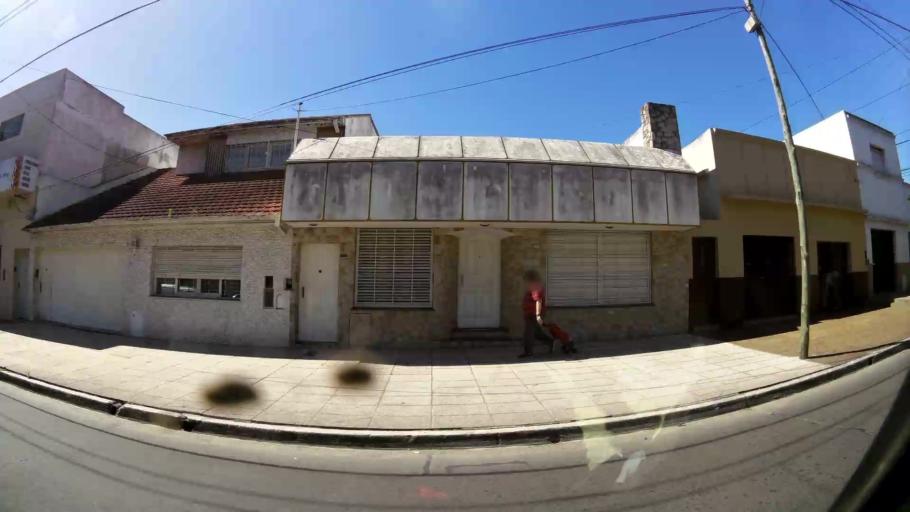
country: AR
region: Buenos Aires
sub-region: Partido de Quilmes
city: Quilmes
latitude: -34.7196
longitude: -58.2955
